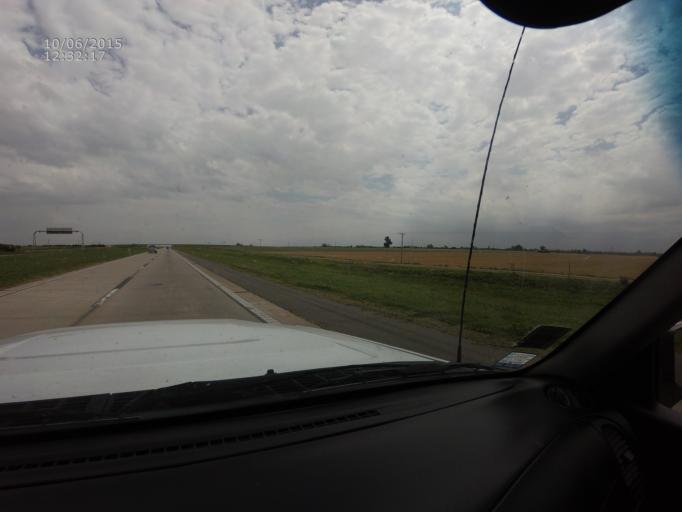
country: AR
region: Santa Fe
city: Carcarana
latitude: -32.8812
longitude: -61.1422
